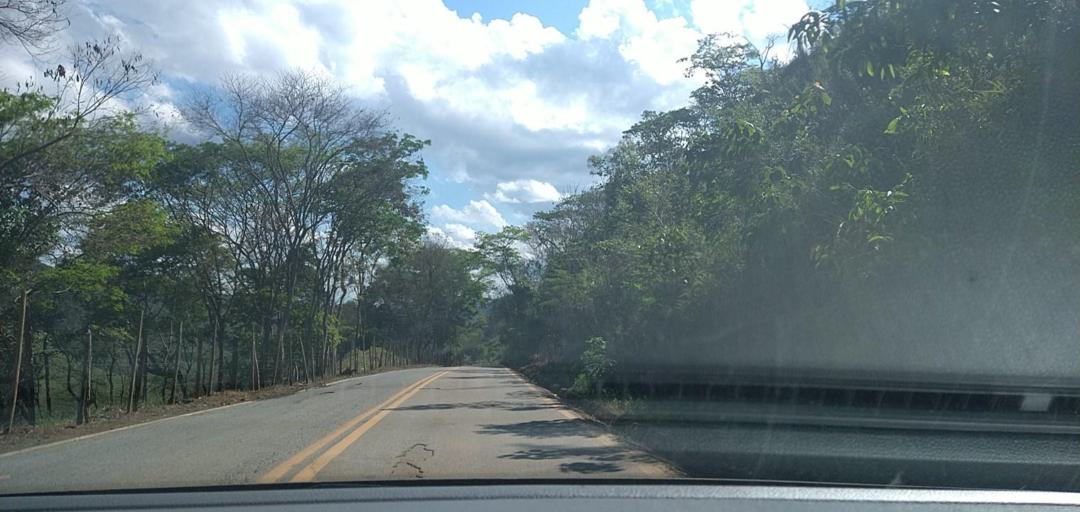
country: BR
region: Minas Gerais
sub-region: Alvinopolis
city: Alvinopolis
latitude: -20.0450
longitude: -43.0337
